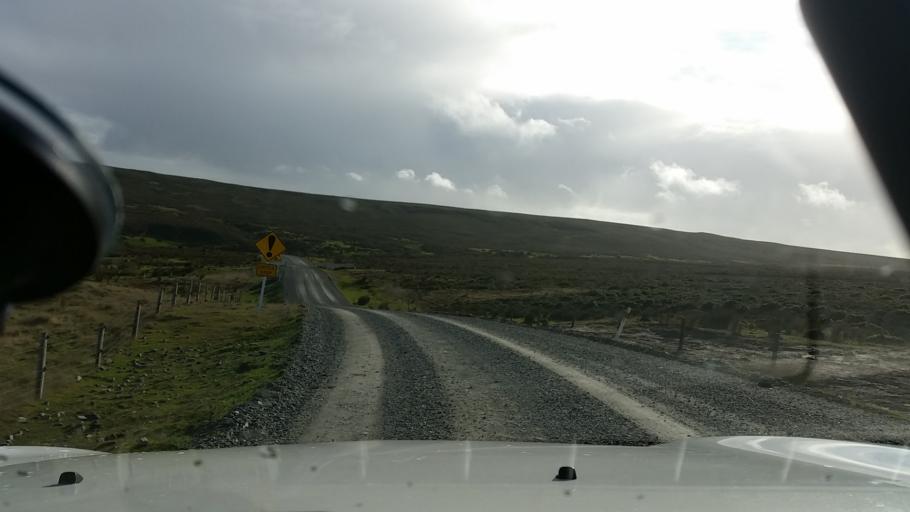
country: NZ
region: Chatham Islands
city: Waitangi
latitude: -43.7966
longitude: -176.6605
